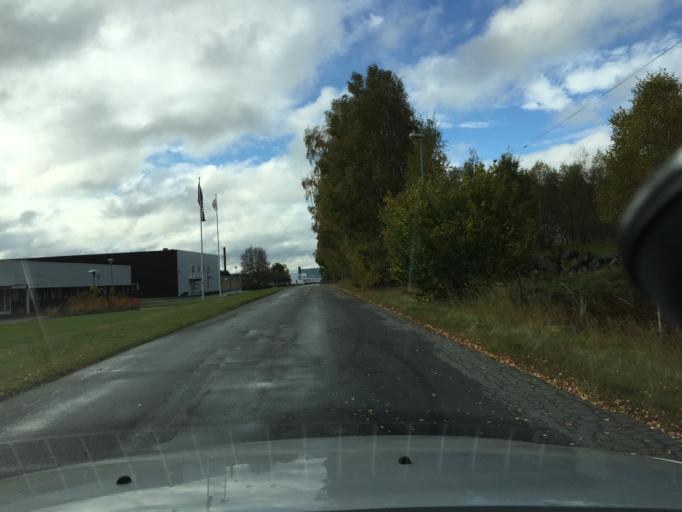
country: SE
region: Skane
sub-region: Hassleholms Kommun
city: Sosdala
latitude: 56.0437
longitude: 13.6905
